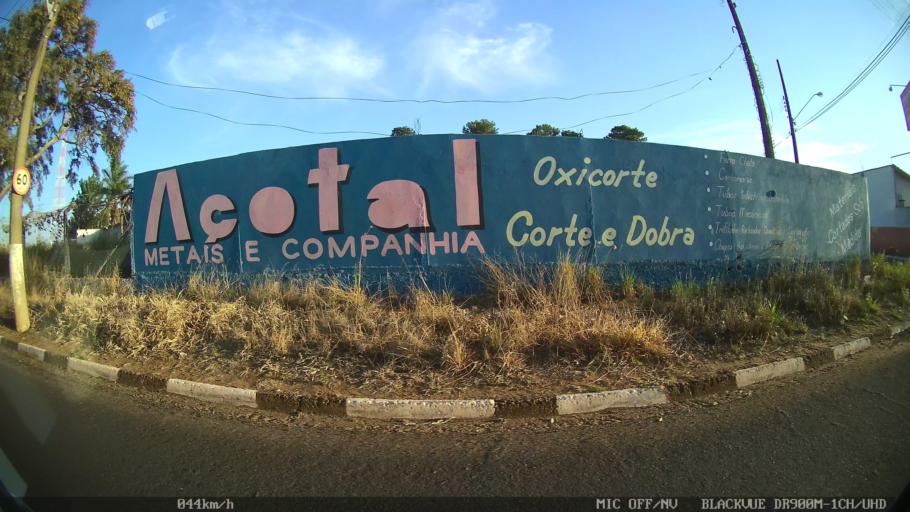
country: BR
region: Sao Paulo
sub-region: Franca
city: Franca
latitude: -20.5138
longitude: -47.3819
